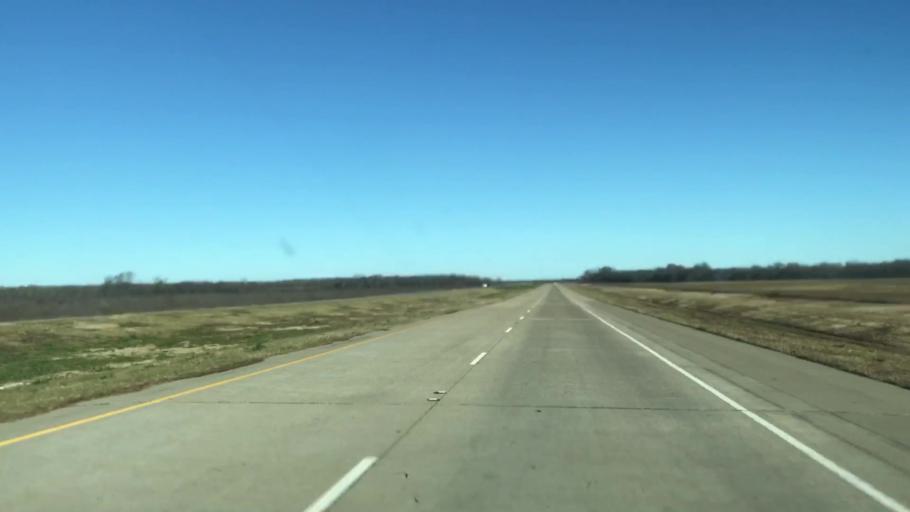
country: US
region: Louisiana
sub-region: Caddo Parish
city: Blanchard
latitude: 32.6323
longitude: -93.8375
